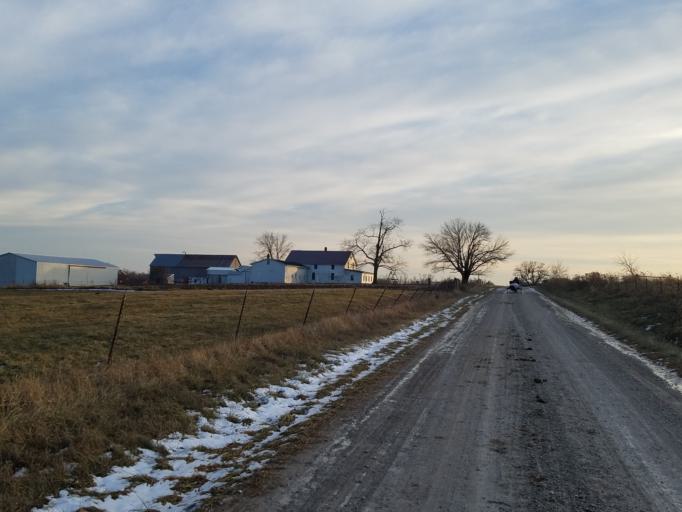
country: US
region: Missouri
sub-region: Randolph County
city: Moberly
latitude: 39.3325
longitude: -92.3030
